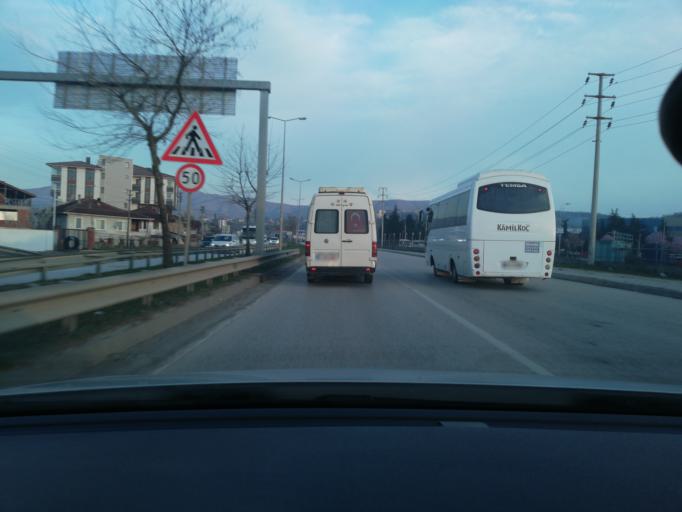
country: TR
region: Duzce
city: Konuralp
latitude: 40.8959
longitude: 31.1660
